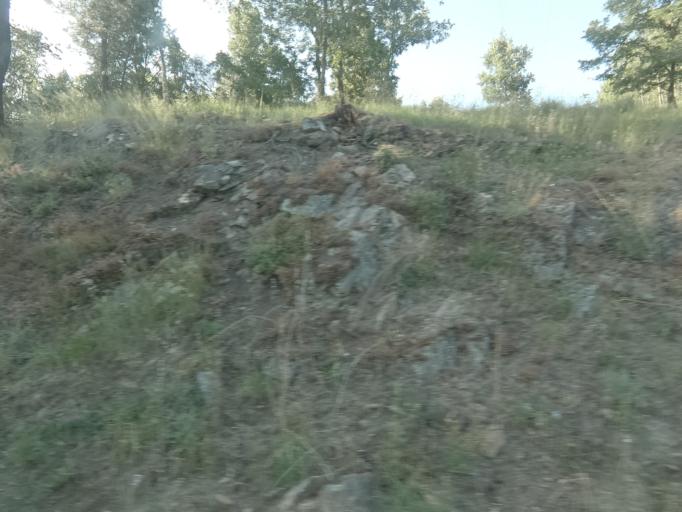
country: PT
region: Vila Real
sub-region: Sabrosa
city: Vilela
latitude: 41.2760
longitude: -7.6651
